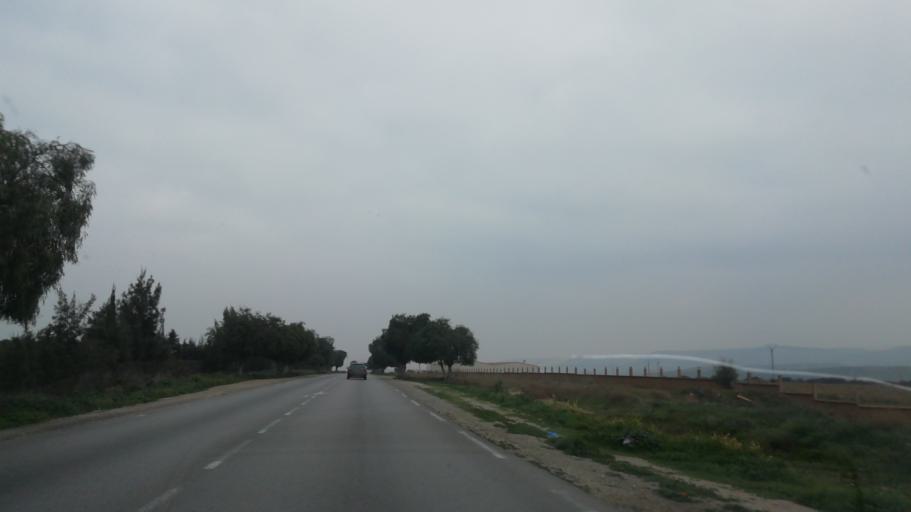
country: DZ
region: Mascara
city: Sig
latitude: 35.5388
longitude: -0.3515
